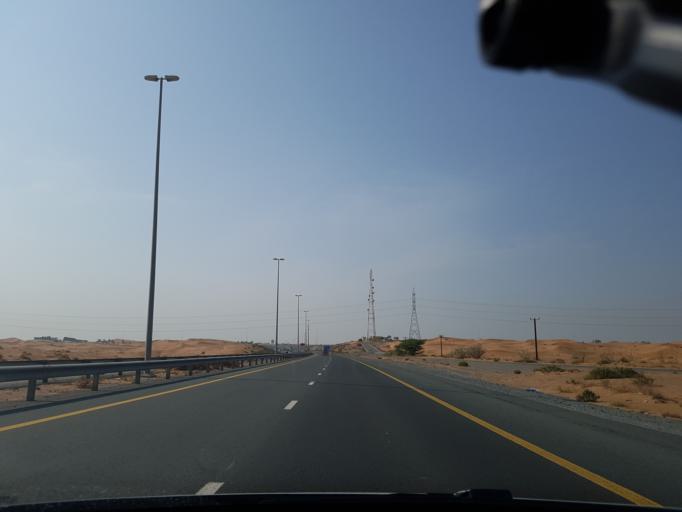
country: AE
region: Umm al Qaywayn
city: Umm al Qaywayn
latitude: 25.5254
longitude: 55.7316
